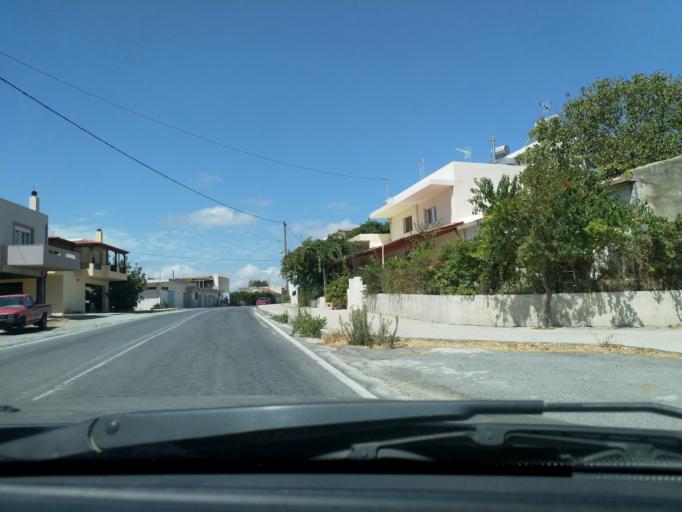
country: GR
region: Crete
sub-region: Nomos Rethymnis
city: Agia Foteini
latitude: 35.1862
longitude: 24.5553
